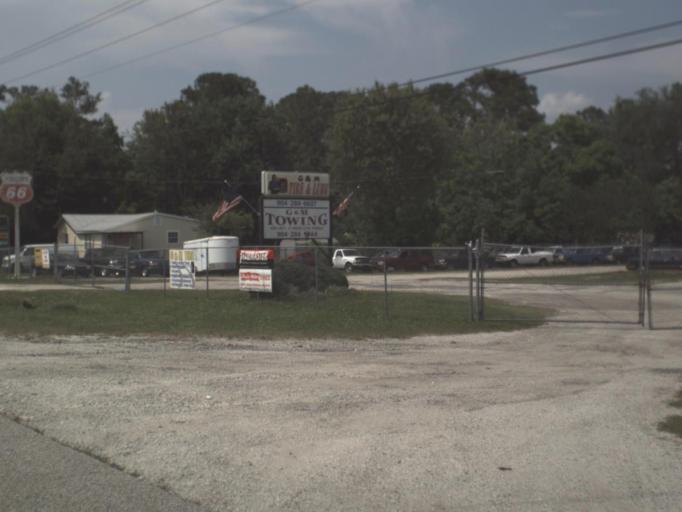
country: US
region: Florida
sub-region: Clay County
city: Green Cove Springs
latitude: 29.9276
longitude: -81.6858
